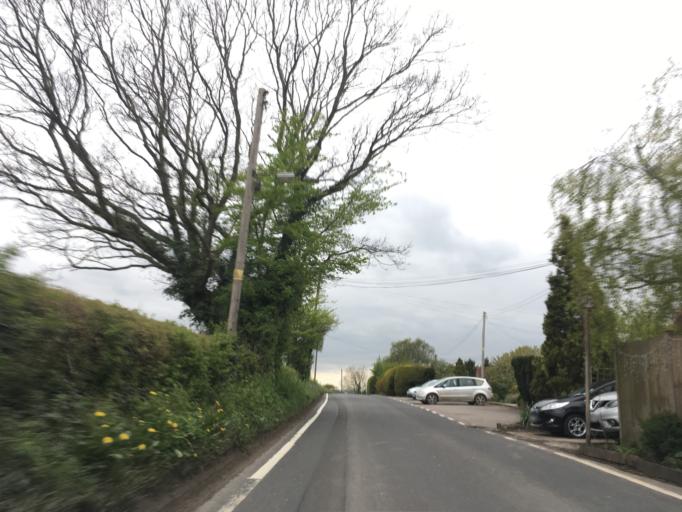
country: GB
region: England
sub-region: Gloucestershire
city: Wotton-under-Edge
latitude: 51.6276
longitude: -2.3718
